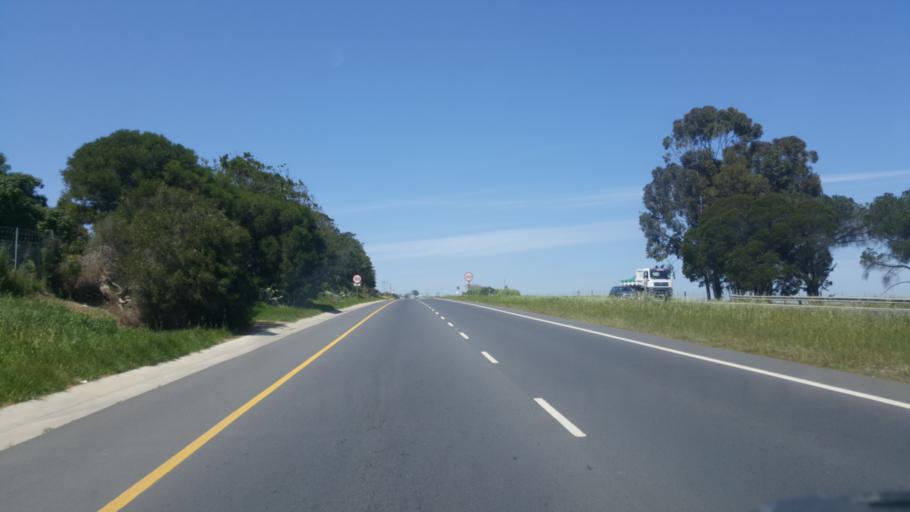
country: ZA
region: Western Cape
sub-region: City of Cape Town
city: Kraaifontein
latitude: -33.9555
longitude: 18.7208
